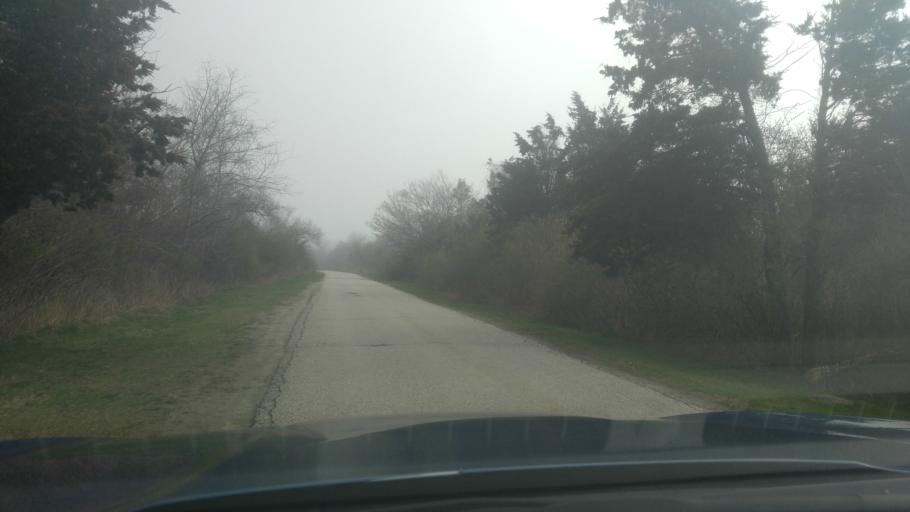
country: US
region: Rhode Island
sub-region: Newport County
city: Jamestown
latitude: 41.4549
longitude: -71.3991
